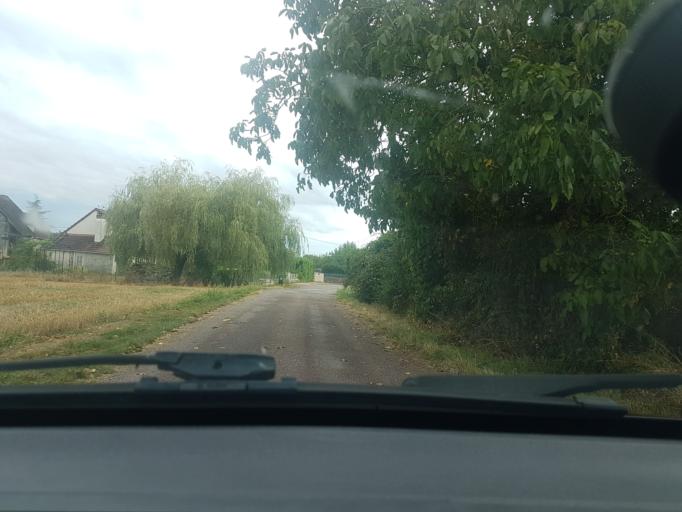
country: FR
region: Bourgogne
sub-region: Departement de Saone-et-Loire
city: Fontaines
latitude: 46.8562
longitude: 4.7602
